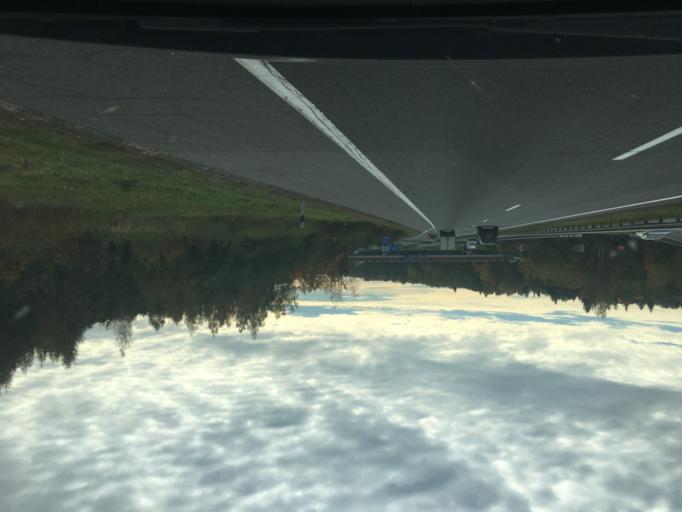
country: BY
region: Minsk
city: Enyerhyetykaw
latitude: 53.5930
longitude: 27.0411
